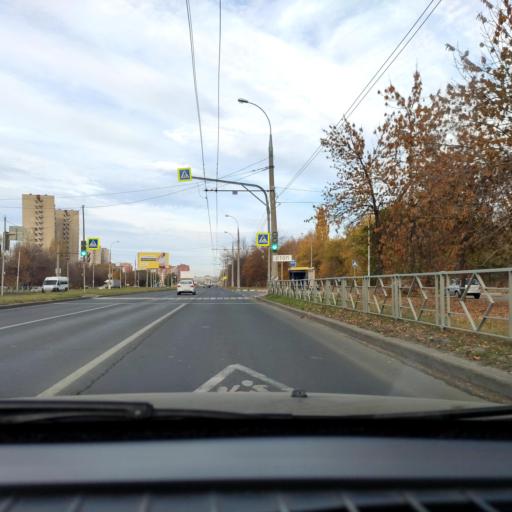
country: RU
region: Samara
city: Tol'yatti
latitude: 53.5059
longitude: 49.3010
